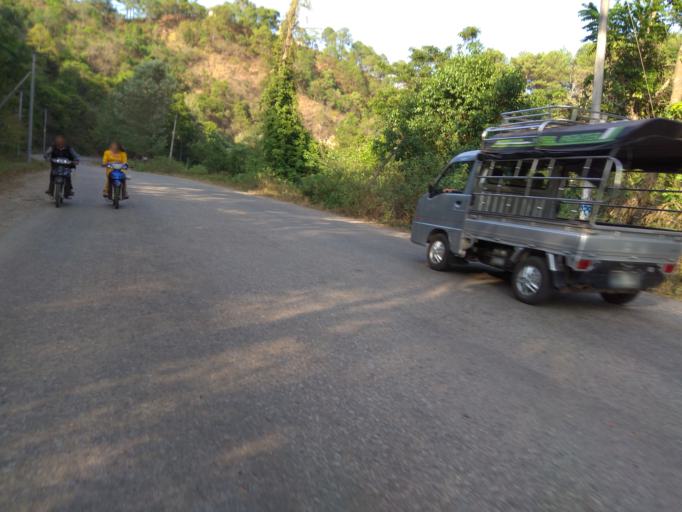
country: MM
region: Shan
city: Taunggyi
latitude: 20.6326
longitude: 96.5817
